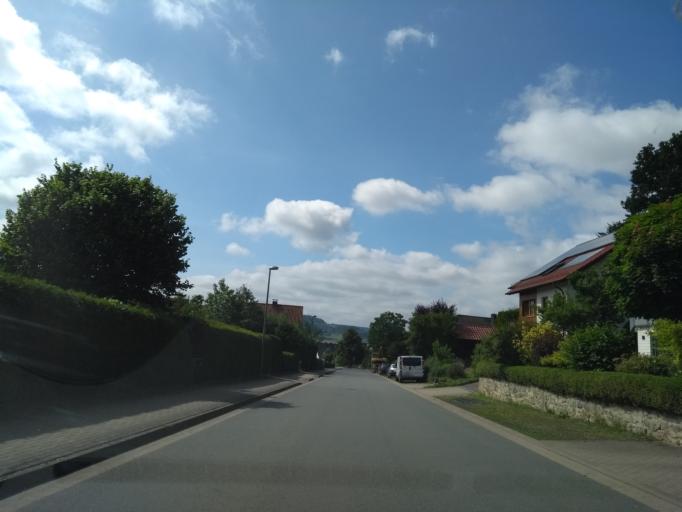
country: DE
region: North Rhine-Westphalia
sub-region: Regierungsbezirk Detmold
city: Lugde
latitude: 51.9593
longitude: 9.2580
